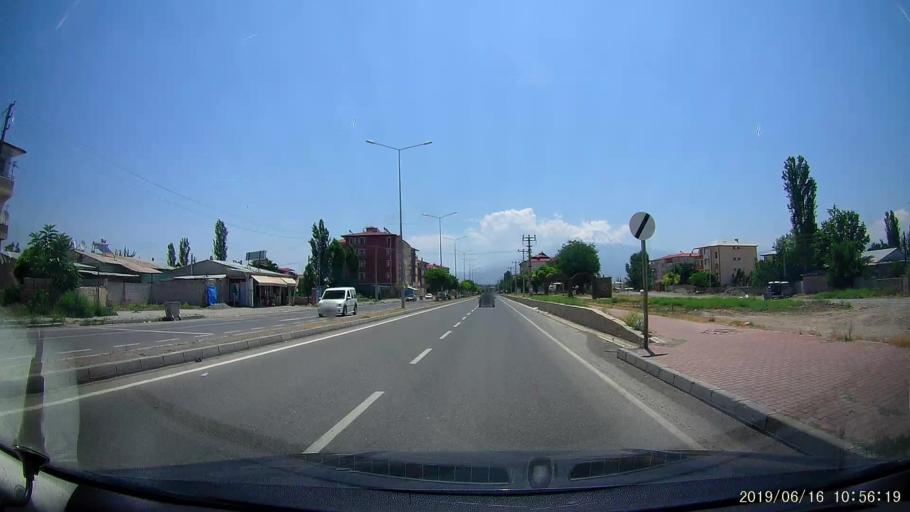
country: TR
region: Igdir
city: Igdir
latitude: 39.9306
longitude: 44.0208
